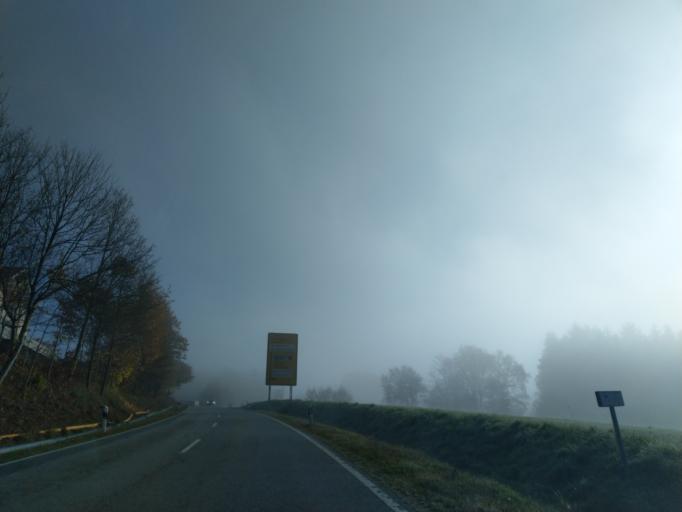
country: DE
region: Bavaria
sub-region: Lower Bavaria
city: Aussernzell
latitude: 48.7196
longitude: 13.2550
